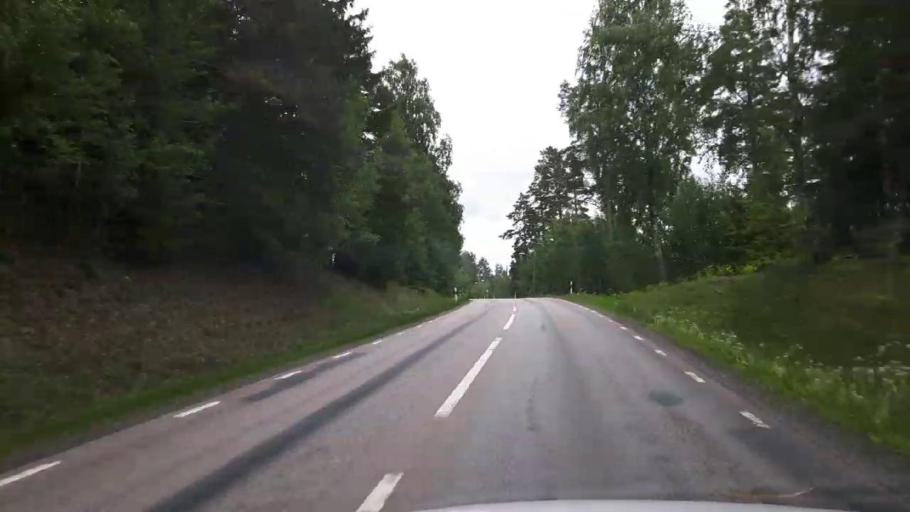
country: SE
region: Vaestmanland
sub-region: Kopings Kommun
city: Kolsva
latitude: 59.6315
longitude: 15.8034
